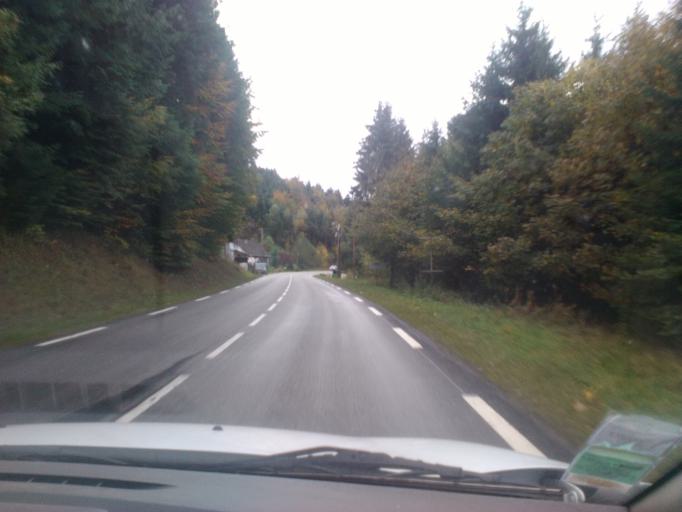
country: FR
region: Lorraine
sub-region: Departement des Vosges
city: Xonrupt-Longemer
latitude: 48.1273
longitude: 6.9152
